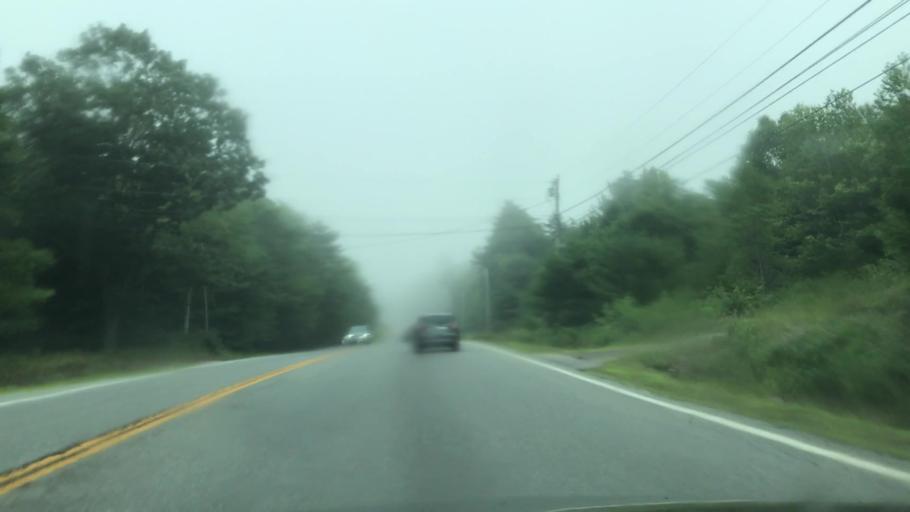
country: US
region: Maine
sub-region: Lincoln County
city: Waldoboro
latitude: 44.0996
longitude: -69.4155
